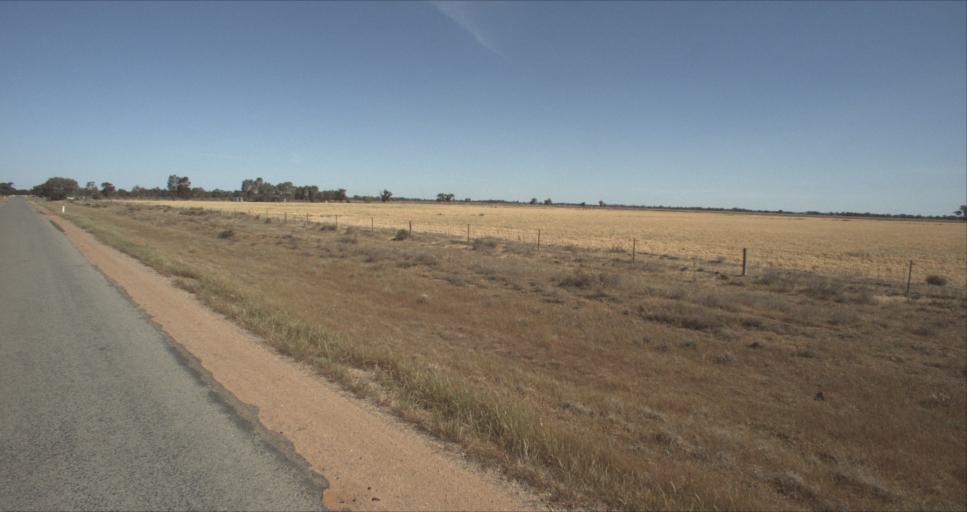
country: AU
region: New South Wales
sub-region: Leeton
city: Leeton
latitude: -34.4953
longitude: 146.3884
